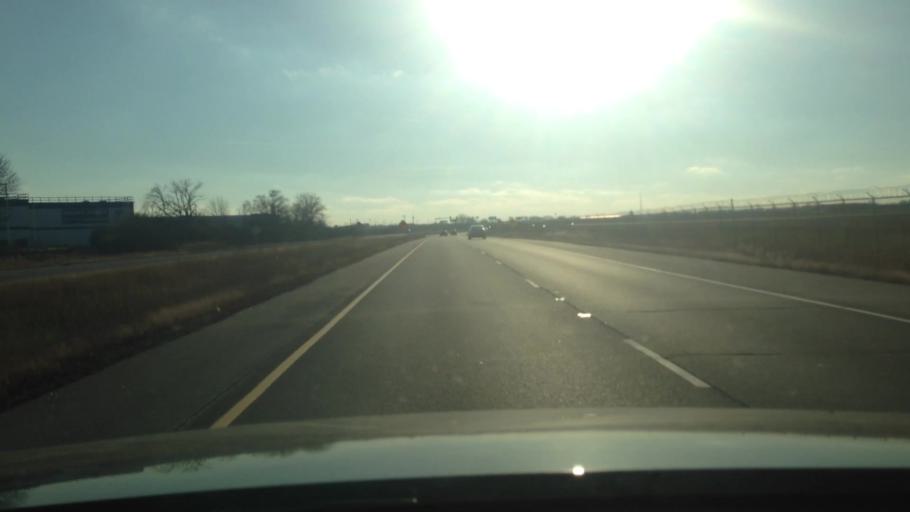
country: US
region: Illinois
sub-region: Cook County
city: Schiller Park
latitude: 41.9549
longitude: -87.8932
